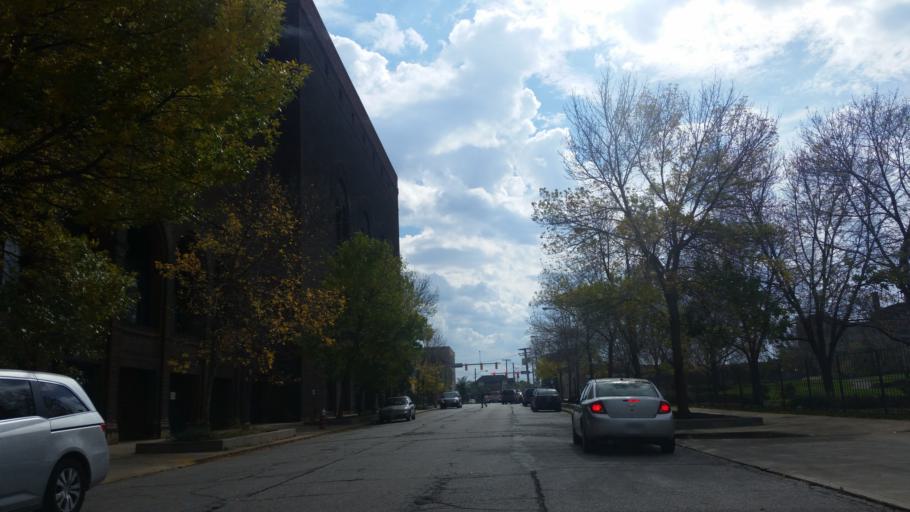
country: US
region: Ohio
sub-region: Cuyahoga County
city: Cleveland
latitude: 41.5043
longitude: -81.6629
